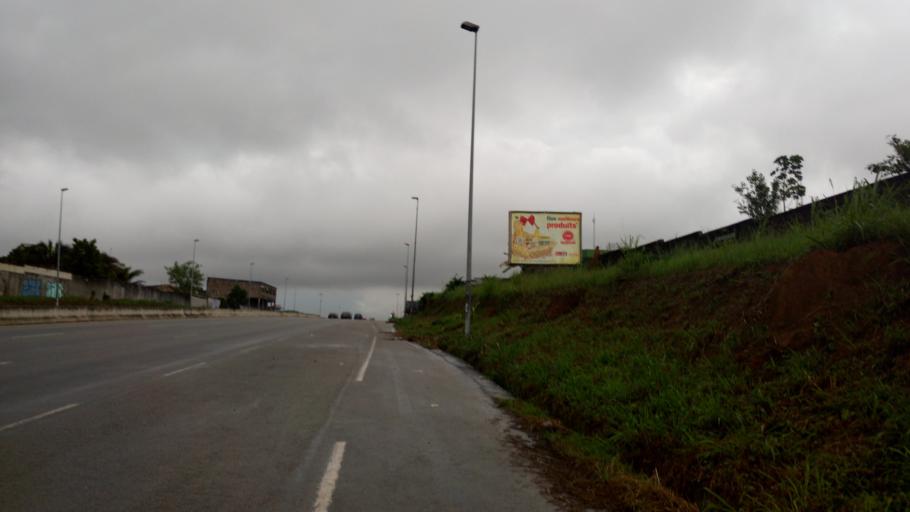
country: CI
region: Lagunes
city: Abidjan
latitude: 5.3514
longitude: -3.9848
